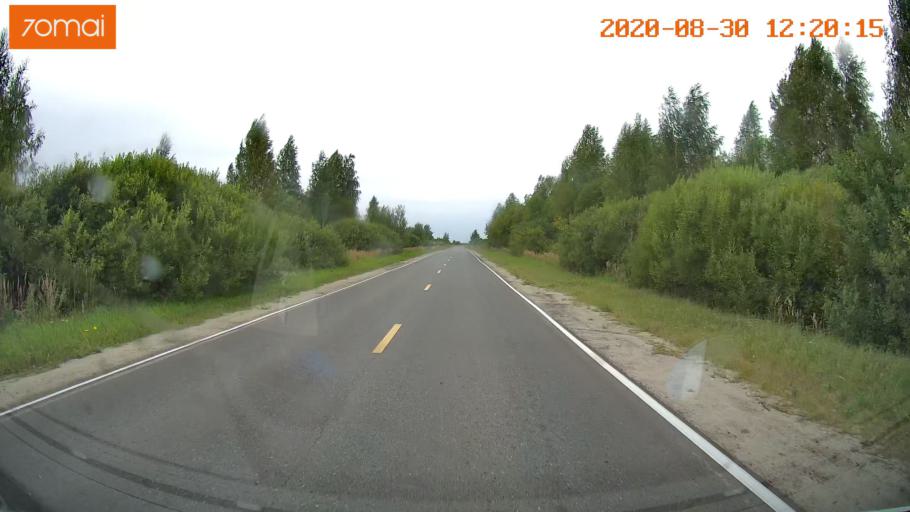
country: RU
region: Ivanovo
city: Yur'yevets
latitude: 57.3228
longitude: 42.9058
